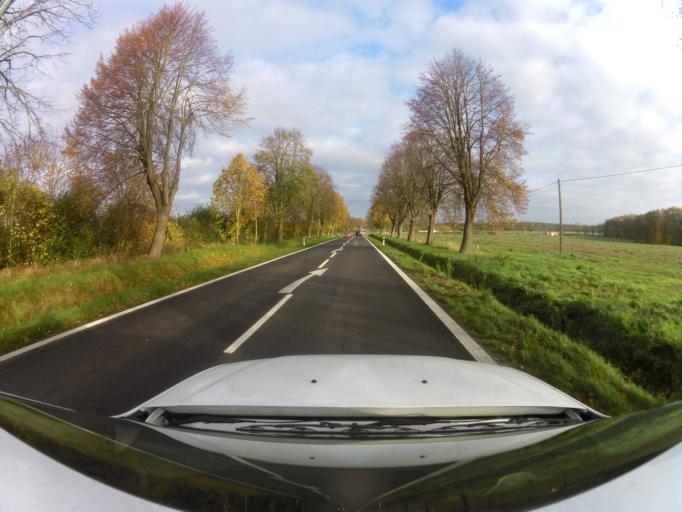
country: PL
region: West Pomeranian Voivodeship
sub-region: Powiat gryficki
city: Trzebiatow
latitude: 54.0036
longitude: 15.2408
